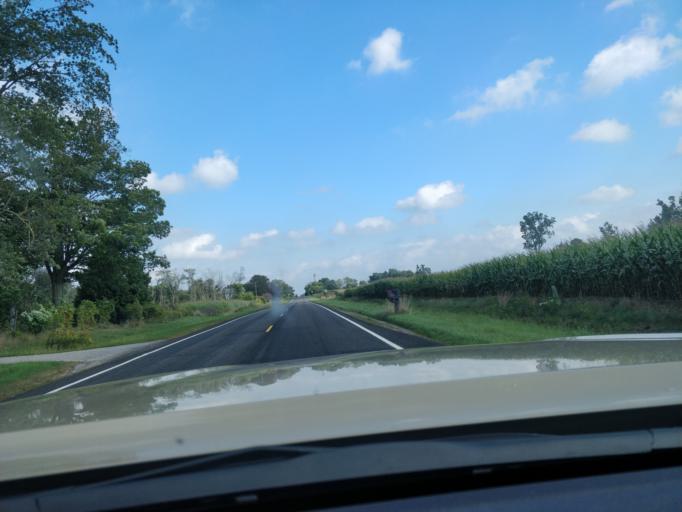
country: US
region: Michigan
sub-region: Ionia County
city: Saranac
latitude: 42.8862
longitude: -85.1813
